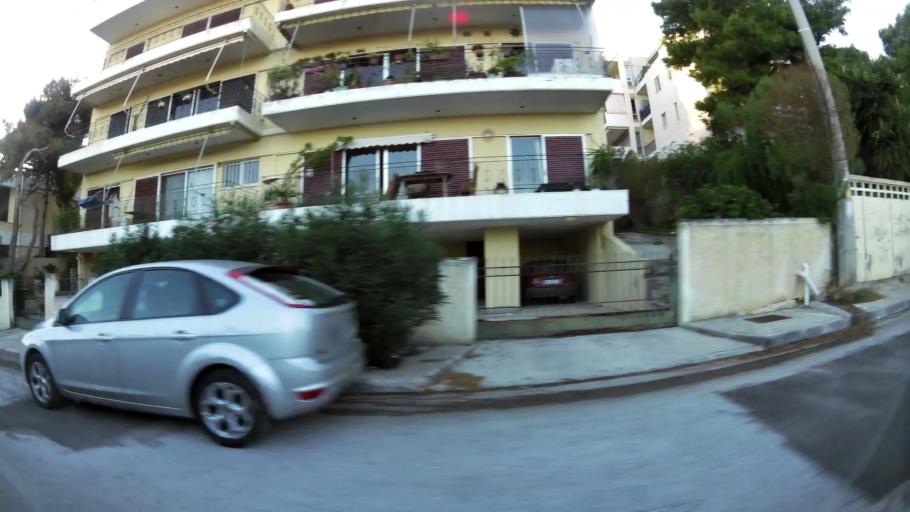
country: GR
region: Attica
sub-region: Nomarchia Anatolikis Attikis
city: Rafina
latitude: 38.0097
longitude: 24.0180
